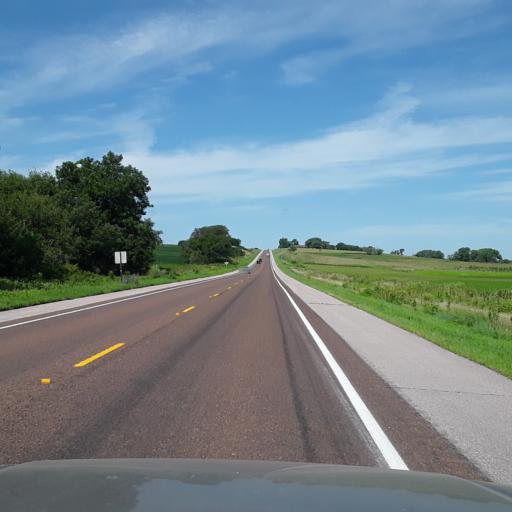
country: US
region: Nebraska
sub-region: Lancaster County
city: Lincoln
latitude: 40.8865
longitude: -96.8358
